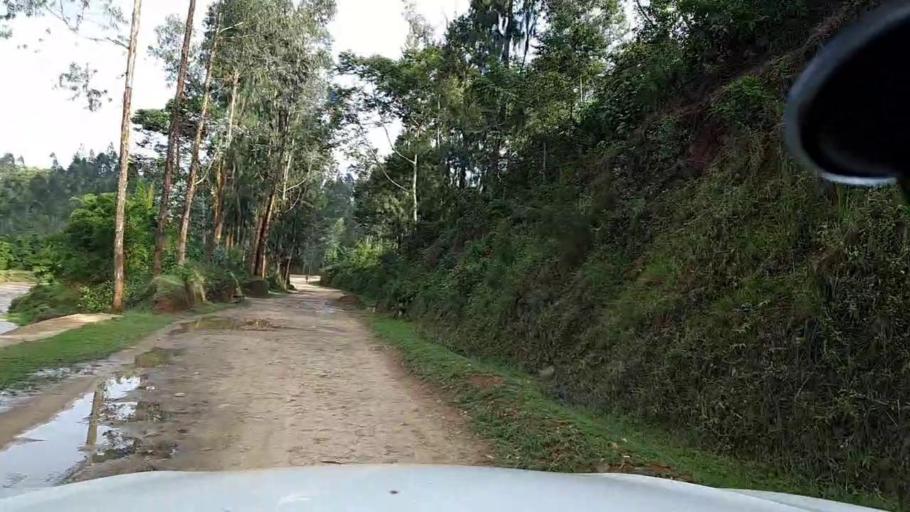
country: RW
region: Western Province
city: Kibuye
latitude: -2.1562
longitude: 29.5453
